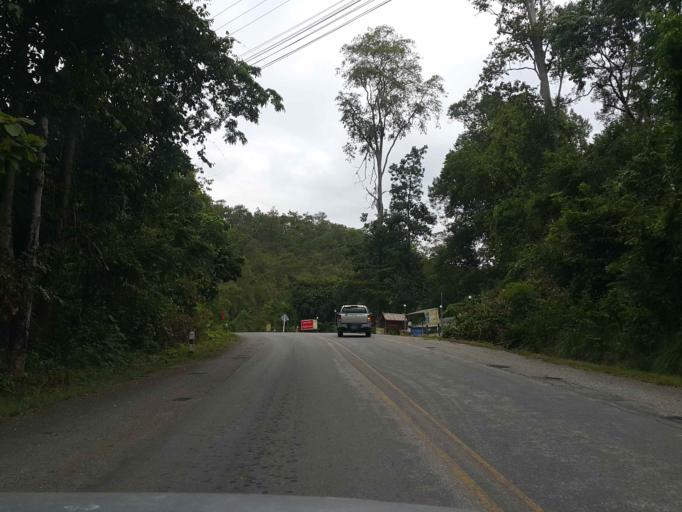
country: TH
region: Lampang
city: Thoen
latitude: 17.6214
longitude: 99.3149
